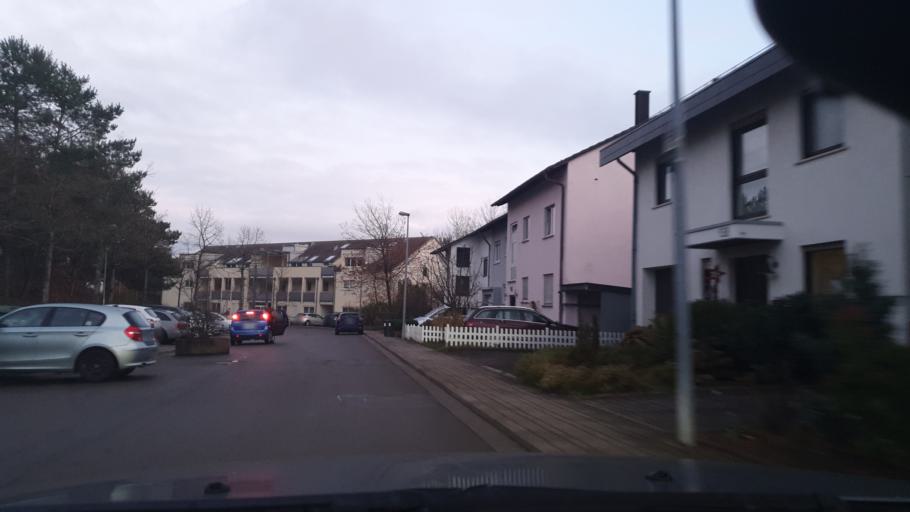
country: DE
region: Rheinland-Pfalz
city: Stelzenberg
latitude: 49.4204
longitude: 7.7371
